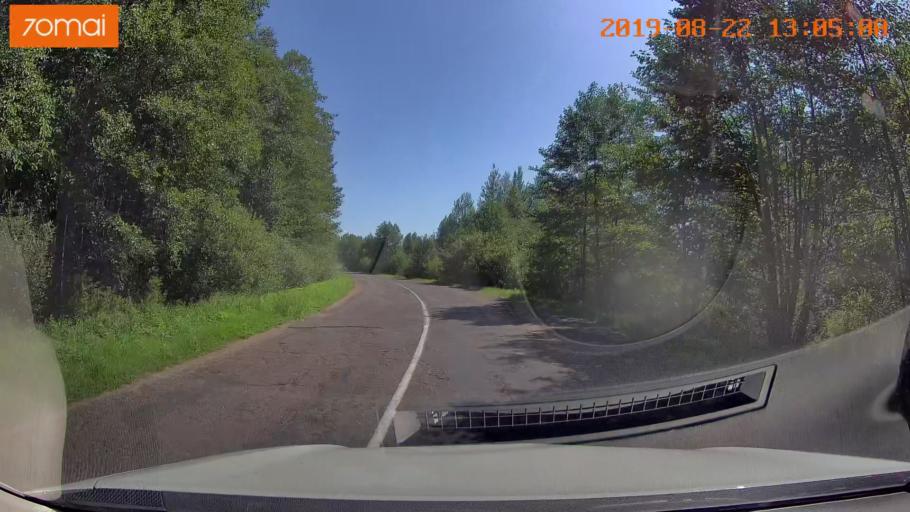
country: BY
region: Minsk
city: Prawdzinski
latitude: 53.3633
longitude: 27.8297
